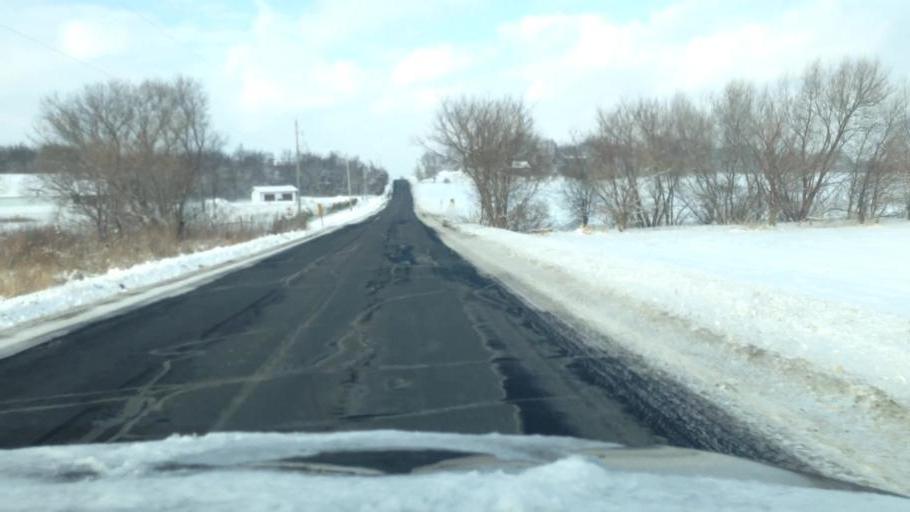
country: US
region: Wisconsin
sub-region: Walworth County
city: East Troy
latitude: 42.7702
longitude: -88.4453
